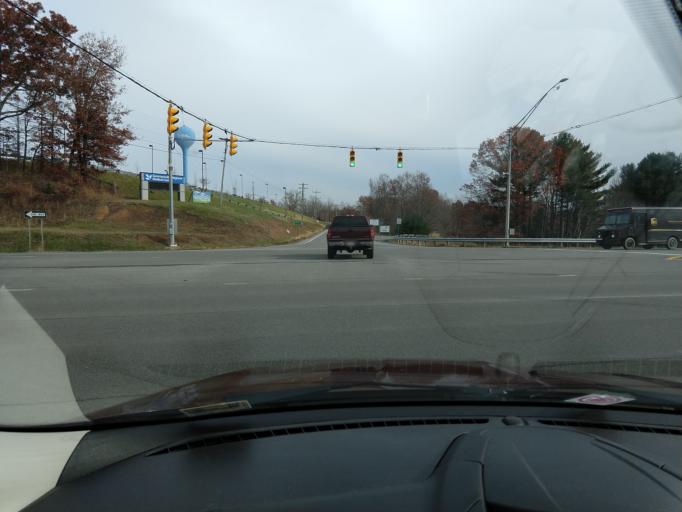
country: US
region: West Virginia
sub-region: Nicholas County
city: Summersville
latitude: 38.2921
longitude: -80.8327
